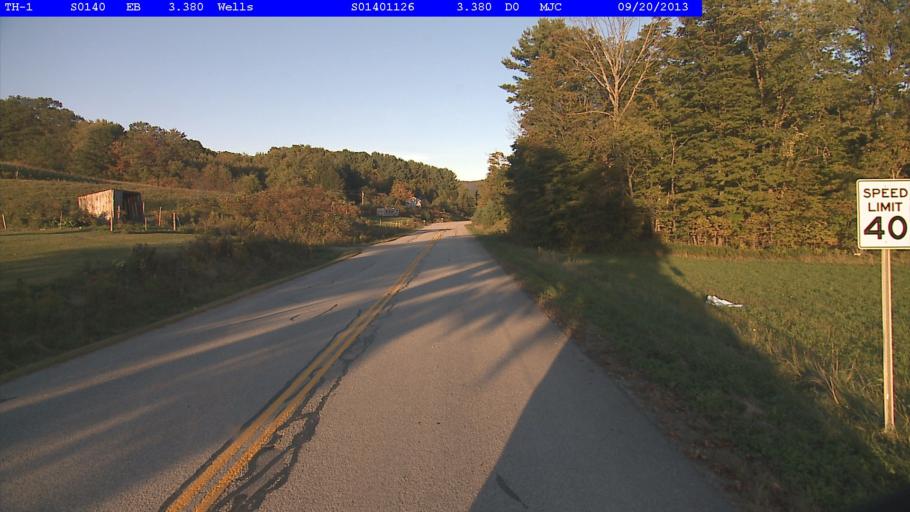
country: US
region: New York
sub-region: Washington County
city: Granville
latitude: 43.4126
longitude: -73.1423
